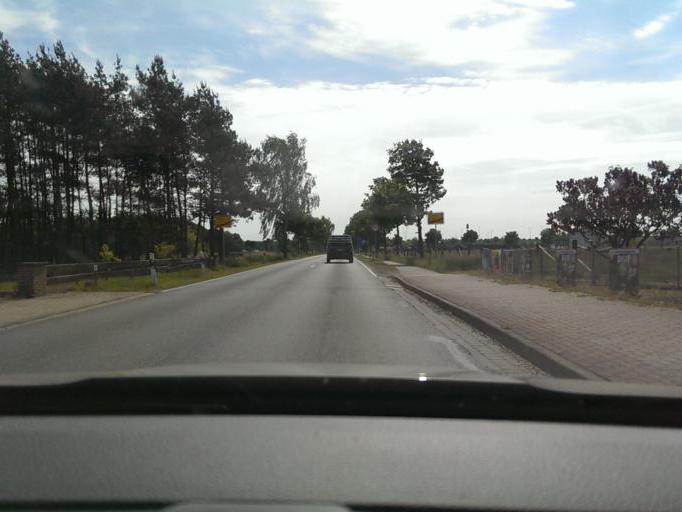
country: DE
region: Lower Saxony
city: Essel
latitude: 52.6763
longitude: 9.6818
